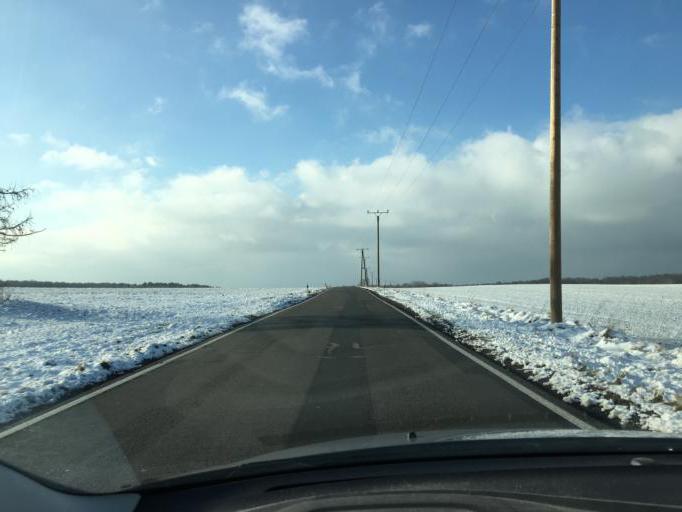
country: DE
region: Saxony
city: Grimma
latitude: 51.2624
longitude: 12.6804
